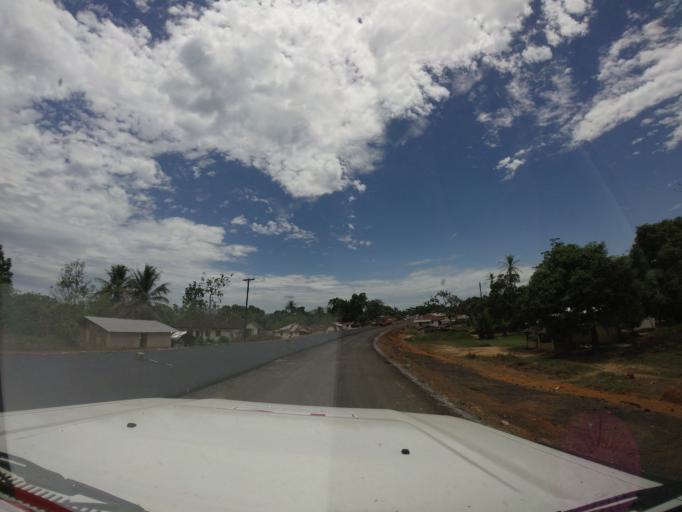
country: LR
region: Margibi
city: Kakata
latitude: 6.7486
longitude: -10.1098
